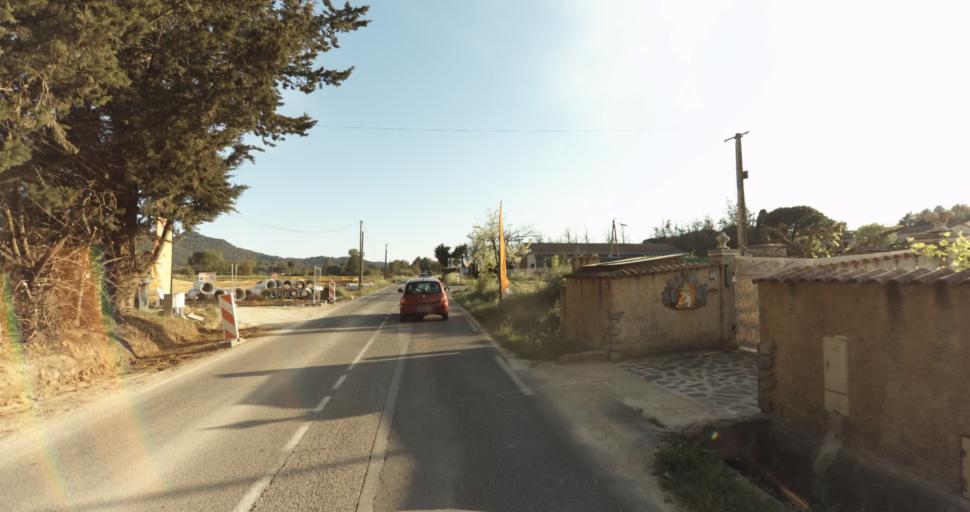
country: FR
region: Provence-Alpes-Cote d'Azur
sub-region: Departement du Var
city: La Crau
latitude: 43.1605
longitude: 6.0985
